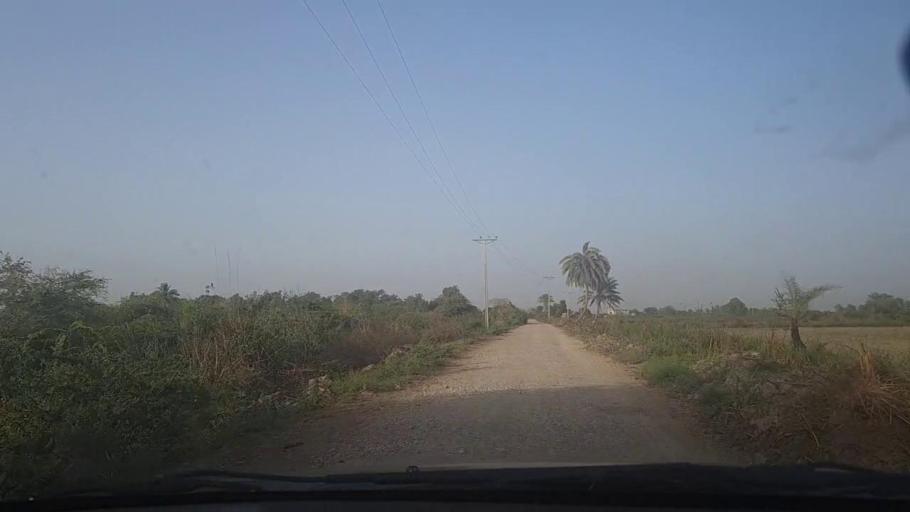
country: PK
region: Sindh
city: Keti Bandar
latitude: 24.2885
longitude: 67.6062
